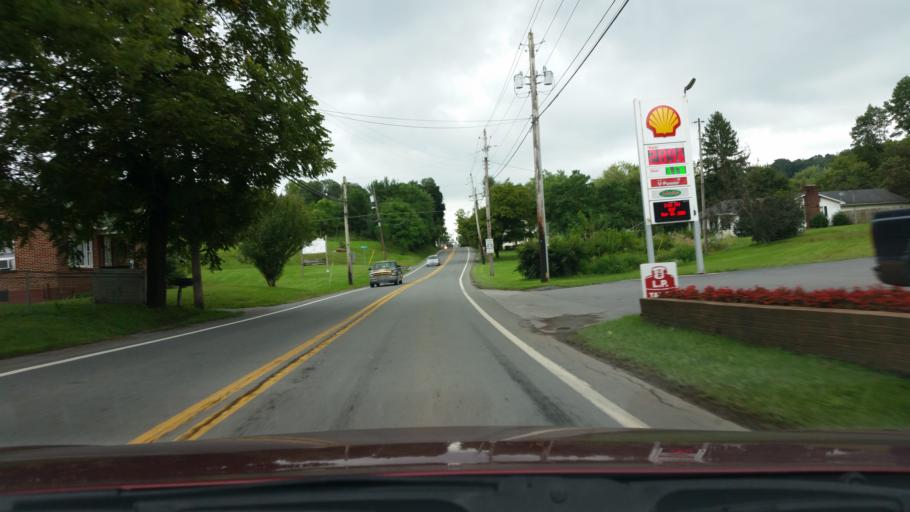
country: US
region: West Virginia
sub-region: Berkeley County
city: Martinsburg
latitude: 39.5572
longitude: -77.9976
